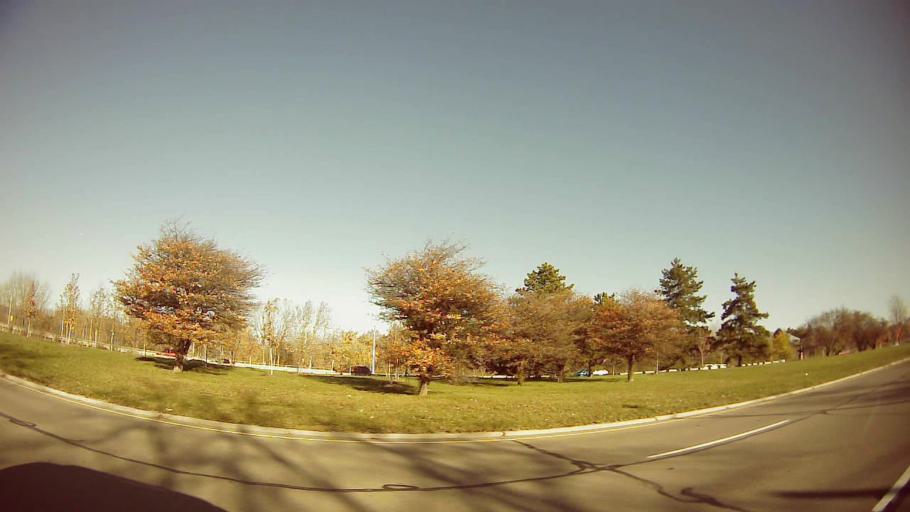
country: US
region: Michigan
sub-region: Wayne County
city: Dearborn Heights
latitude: 42.3275
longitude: -83.2421
